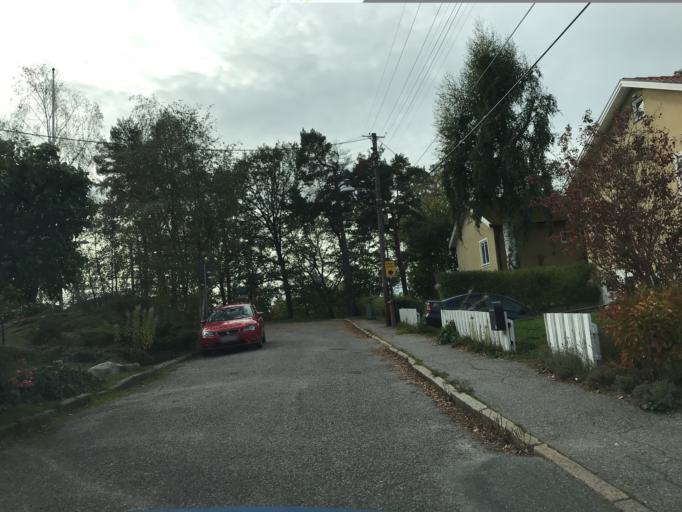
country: SE
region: Stockholm
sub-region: Huddinge Kommun
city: Huddinge
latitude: 59.2740
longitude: 17.9728
